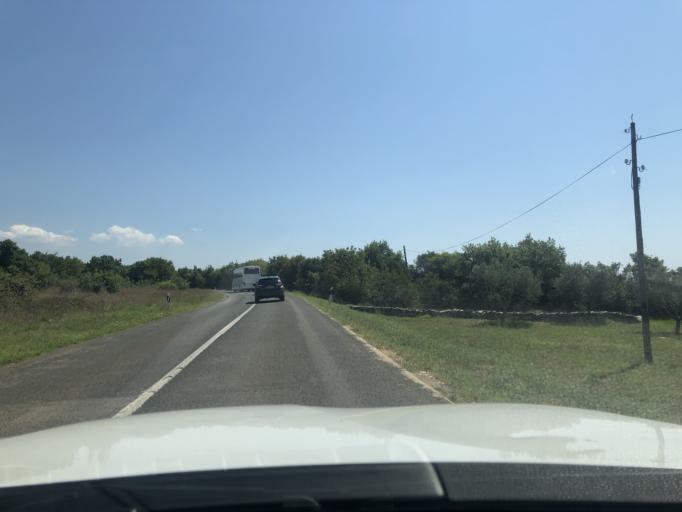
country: HR
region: Istarska
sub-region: Grad Rovinj
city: Rovinj
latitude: 45.0425
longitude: 13.7515
